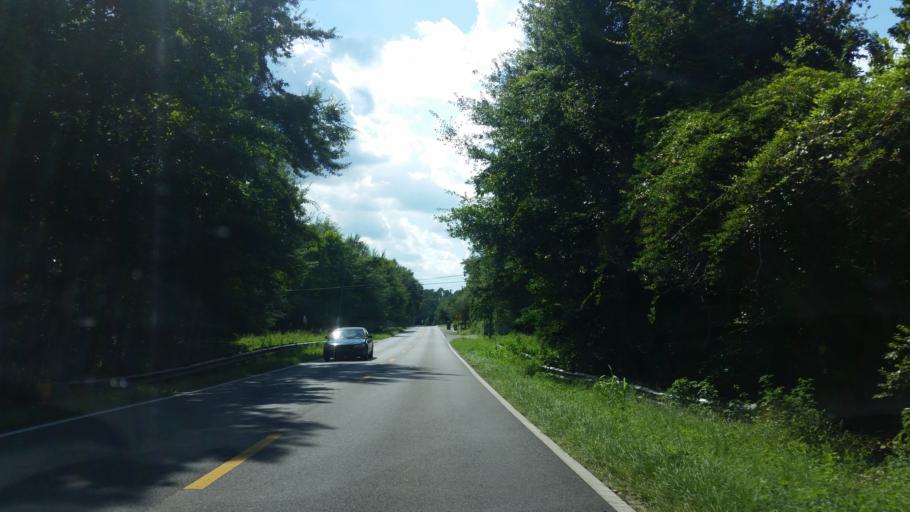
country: US
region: Florida
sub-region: Santa Rosa County
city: Pace
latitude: 30.5922
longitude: -87.1701
